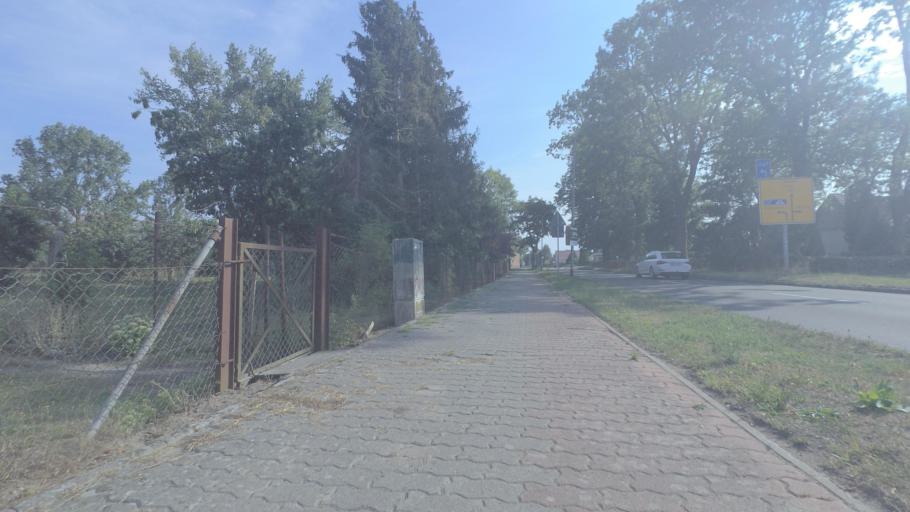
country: DE
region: Mecklenburg-Vorpommern
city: Grimmen
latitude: 54.0566
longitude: 13.1192
